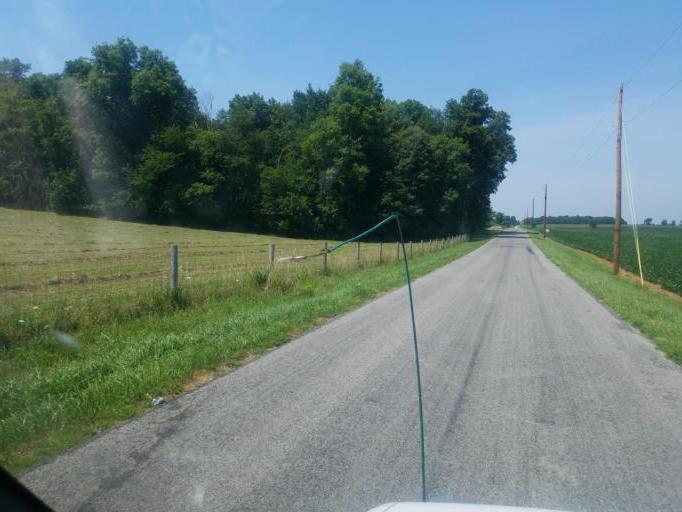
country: US
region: Ohio
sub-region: Logan County
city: West Liberty
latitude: 40.2903
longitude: -83.7980
